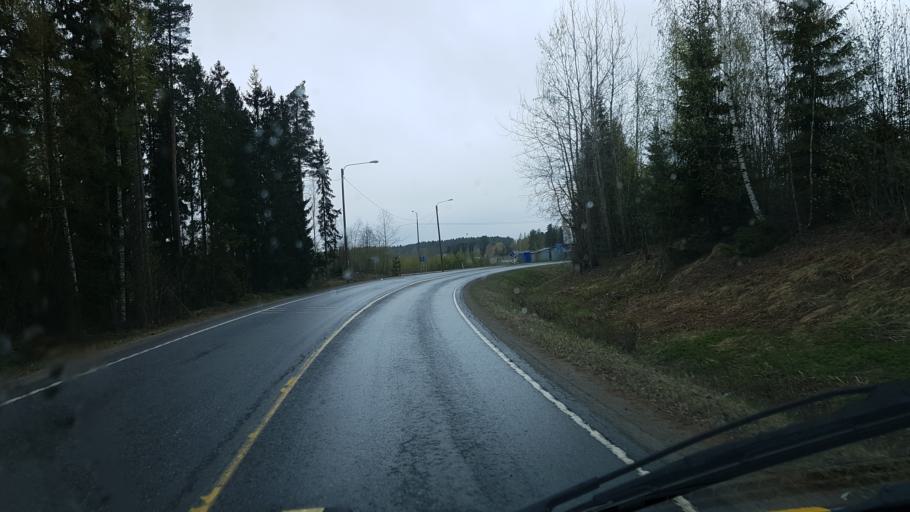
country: FI
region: Pirkanmaa
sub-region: Tampere
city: Pirkkala
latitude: 61.4295
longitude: 23.6228
